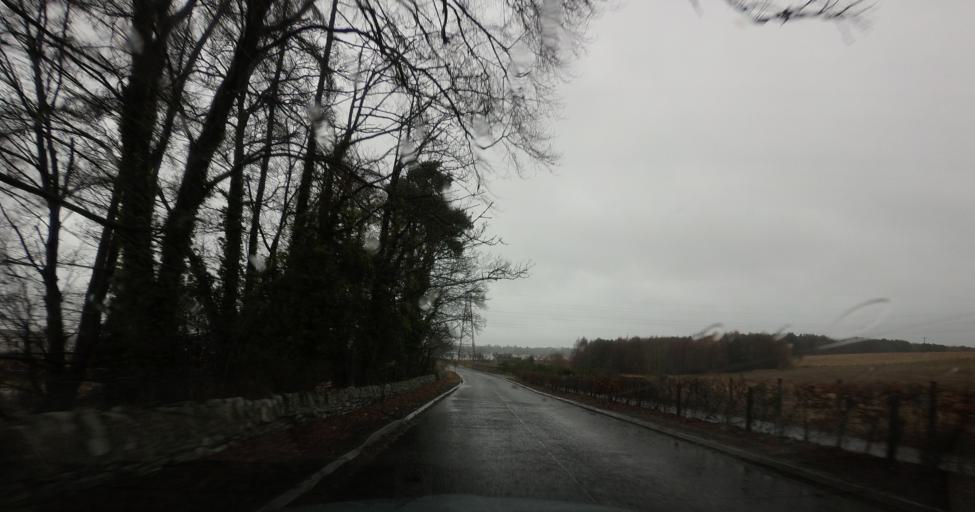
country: GB
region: Scotland
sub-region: Angus
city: Muirhead
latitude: 56.4689
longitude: -3.0669
